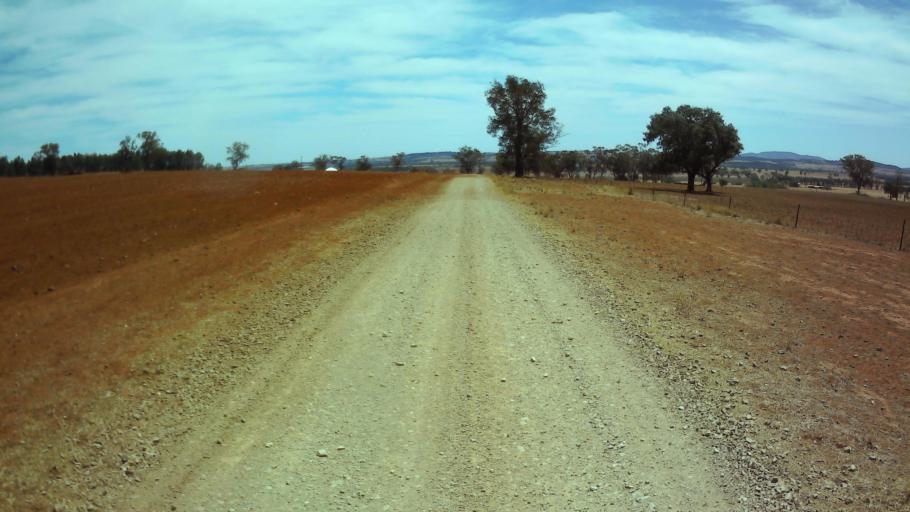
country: AU
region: New South Wales
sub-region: Weddin
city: Grenfell
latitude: -33.7494
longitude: 148.1612
